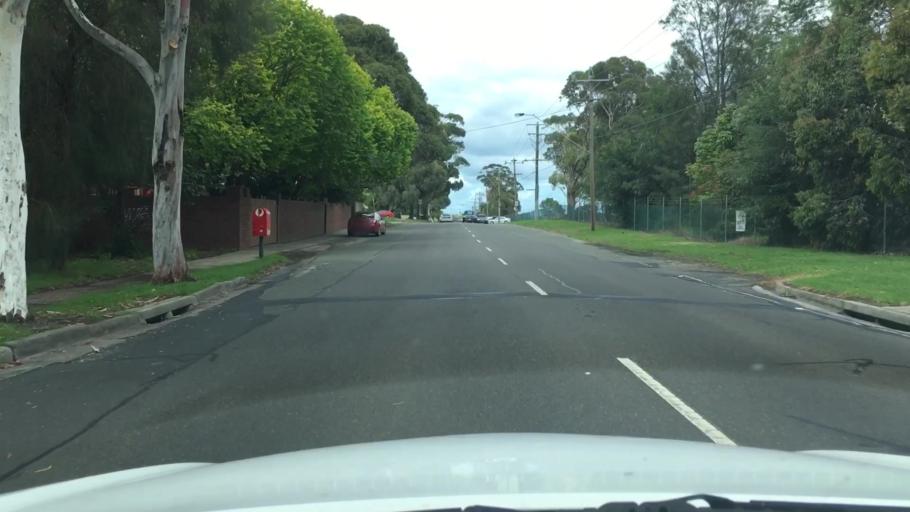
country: AU
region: Victoria
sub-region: Kingston
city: Dingley Village
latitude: -37.9688
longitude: 145.1244
